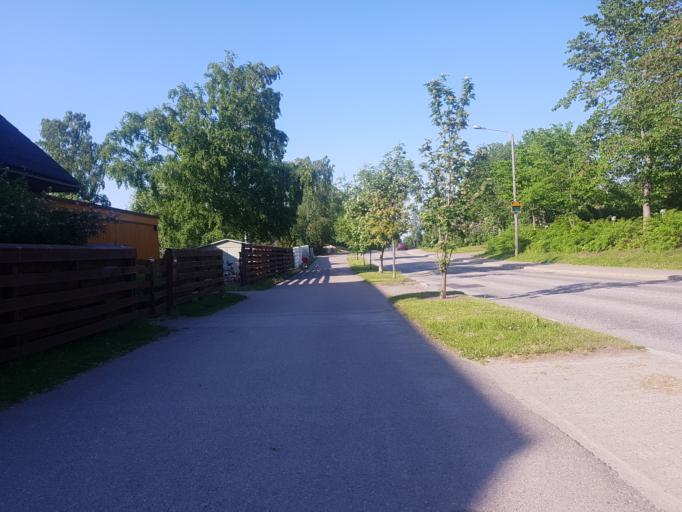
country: FI
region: Uusimaa
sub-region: Helsinki
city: Vantaa
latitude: 60.2644
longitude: 25.0131
